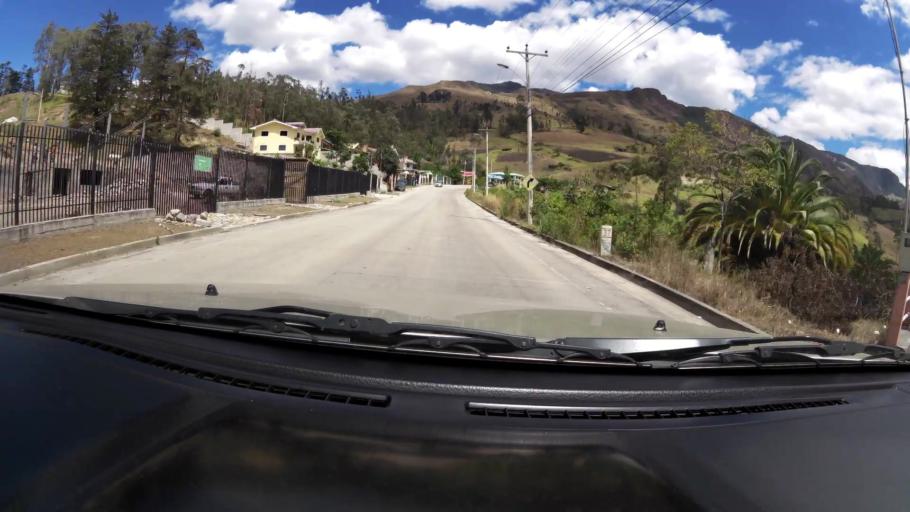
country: EC
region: Azuay
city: Cuenca
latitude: -3.1518
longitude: -79.1464
